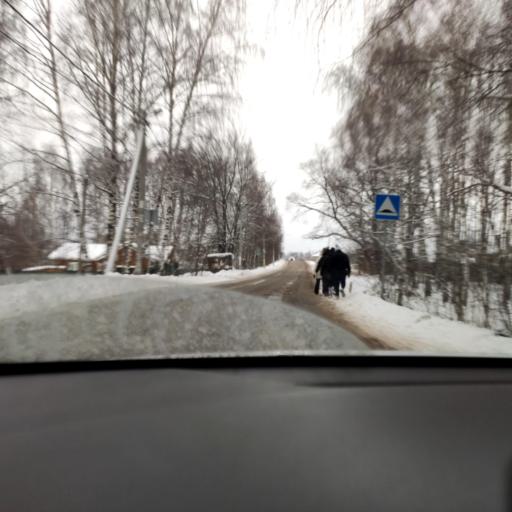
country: RU
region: Tatarstan
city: Osinovo
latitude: 55.8555
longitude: 48.8209
